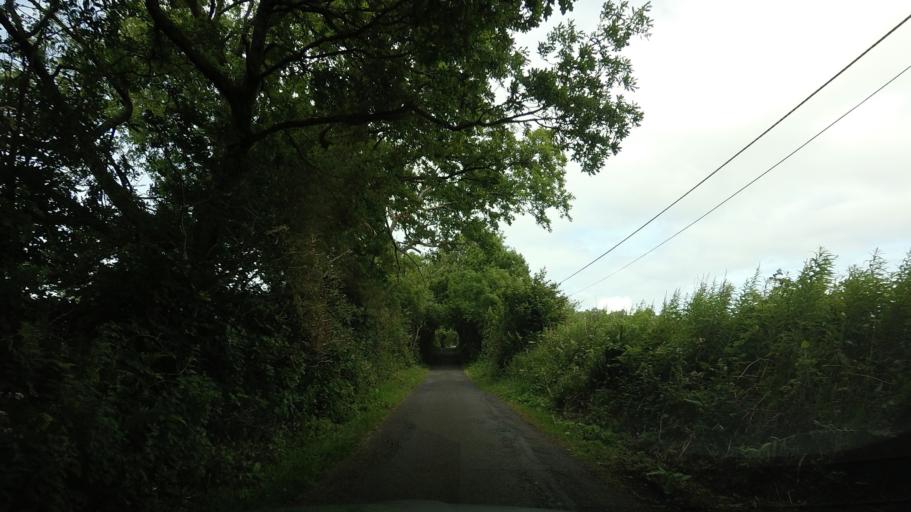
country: GB
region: Scotland
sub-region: Stirling
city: Killearn
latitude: 56.0778
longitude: -4.4500
